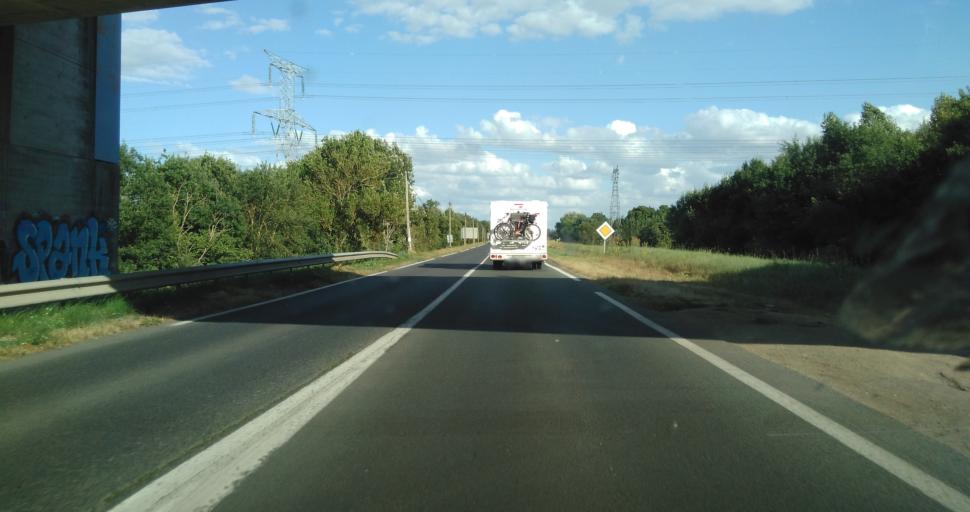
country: FR
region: Centre
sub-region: Departement d'Indre-et-Loire
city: Vouvray
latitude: 47.4030
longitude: 0.8082
